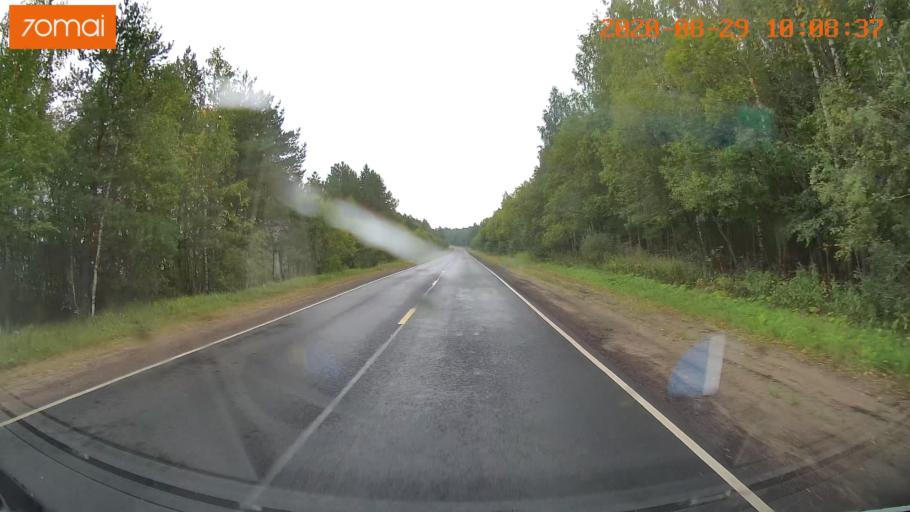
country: RU
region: Ivanovo
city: Kuznechikha
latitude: 57.3754
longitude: 42.5946
